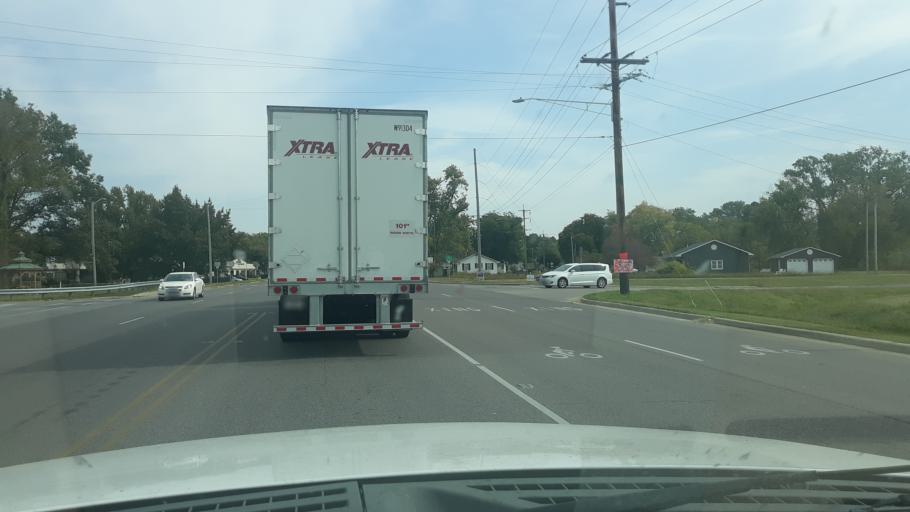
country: US
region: Illinois
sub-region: Saline County
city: Eldorado
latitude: 37.8087
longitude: -88.4350
